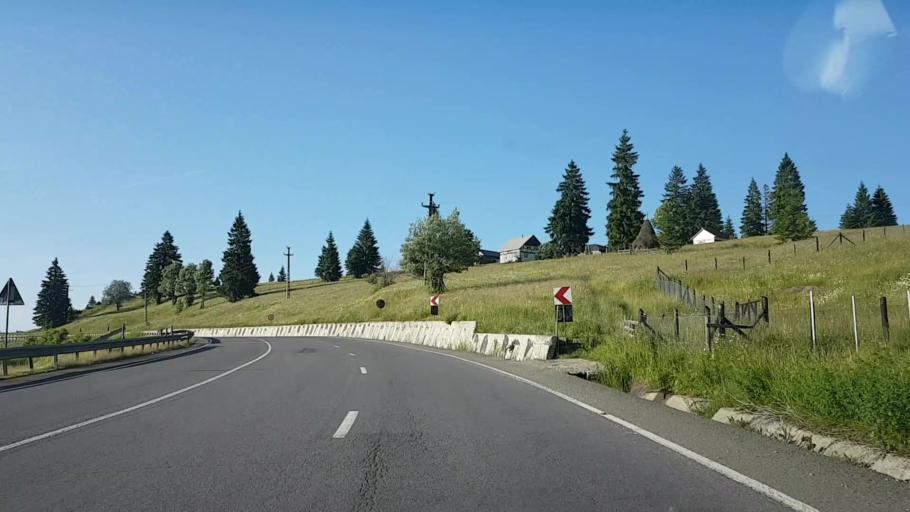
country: RO
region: Bistrita-Nasaud
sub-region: Comuna Lunca Ilvei
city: Lunca Ilvei
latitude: 47.2447
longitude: 25.0210
